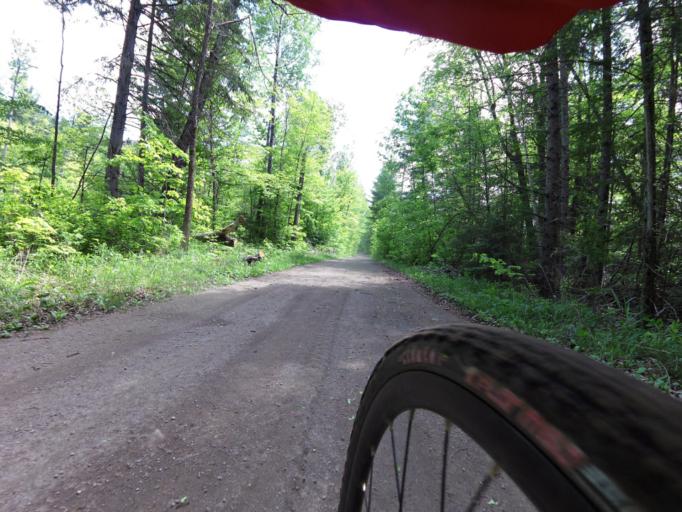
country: CA
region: Ontario
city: Renfrew
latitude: 45.2129
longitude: -76.6924
